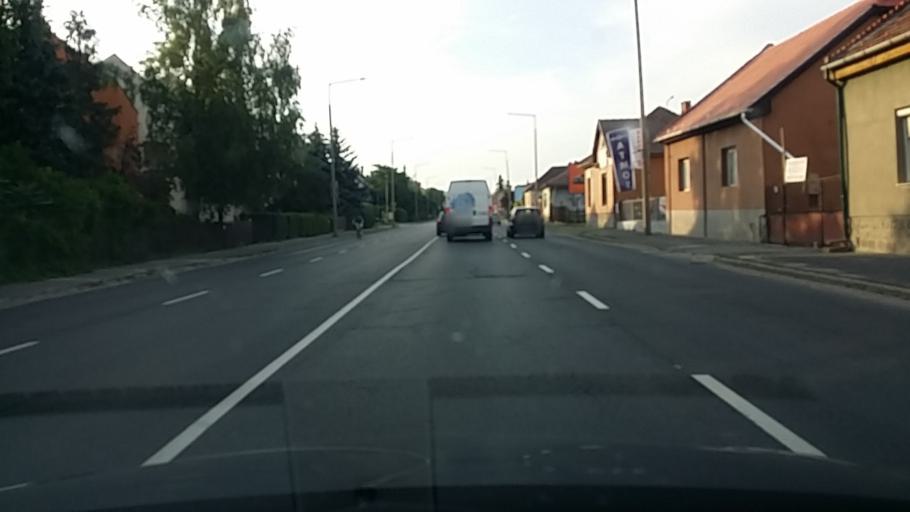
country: HU
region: Borsod-Abauj-Zemplen
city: Miskolc
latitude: 48.0685
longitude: 20.7913
